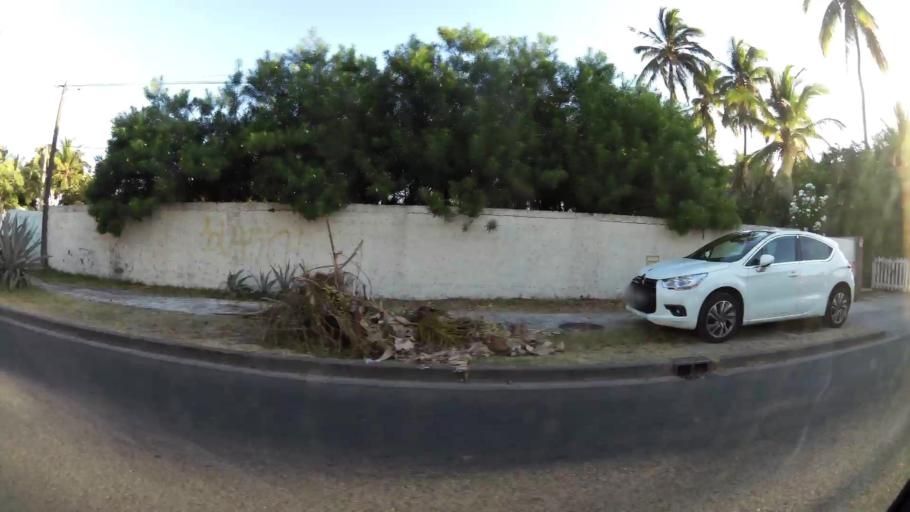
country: RE
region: Reunion
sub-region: Reunion
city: Trois-Bassins
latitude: -21.0984
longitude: 55.2417
